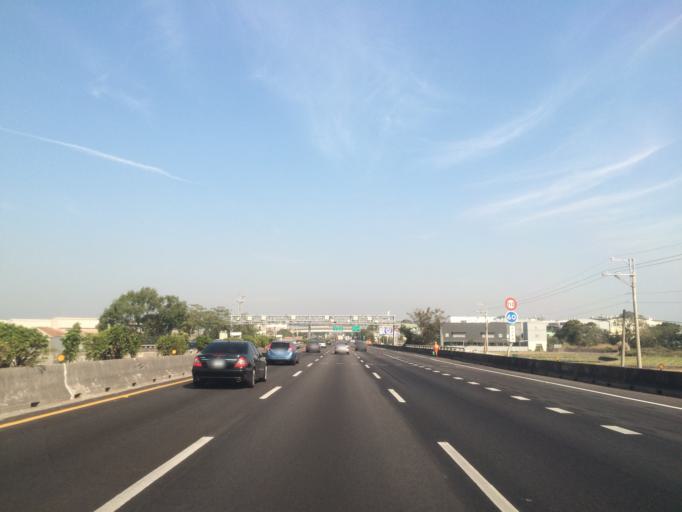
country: TW
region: Taiwan
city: Fengyuan
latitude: 24.2612
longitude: 120.6917
